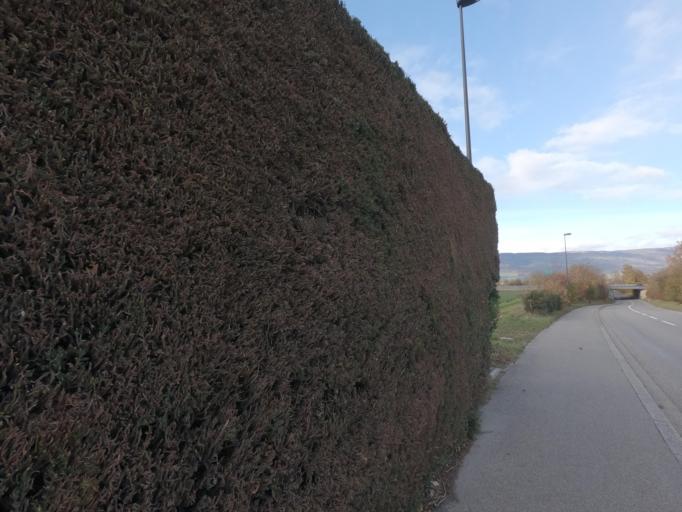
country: CH
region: Solothurn
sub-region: Bezirk Wasseramt
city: Luterbach
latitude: 47.2079
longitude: 7.5848
